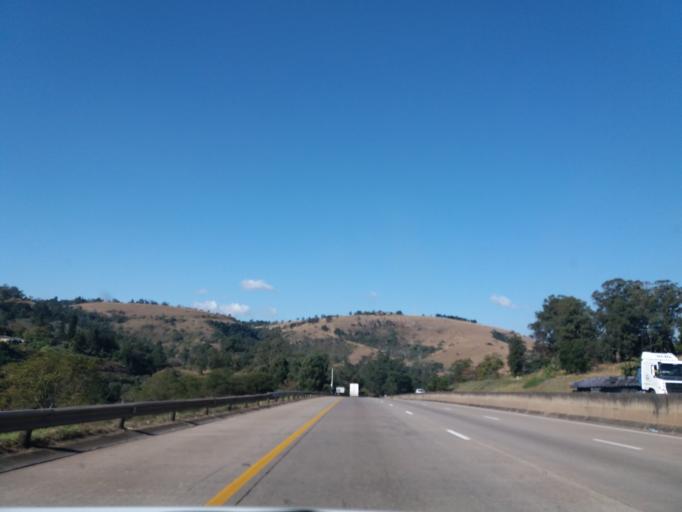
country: ZA
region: KwaZulu-Natal
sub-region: eThekwini Metropolitan Municipality
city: Mpumalanga
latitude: -29.7396
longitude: 30.6565
